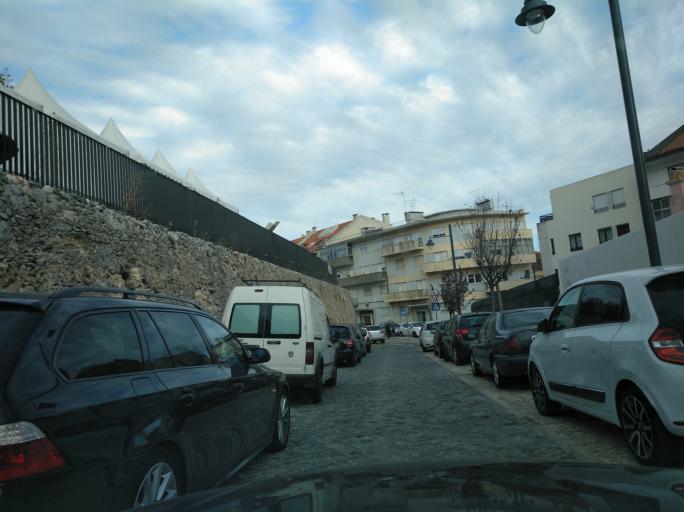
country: PT
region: Lisbon
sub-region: Oeiras
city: Alges
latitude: 38.7025
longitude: -9.2019
